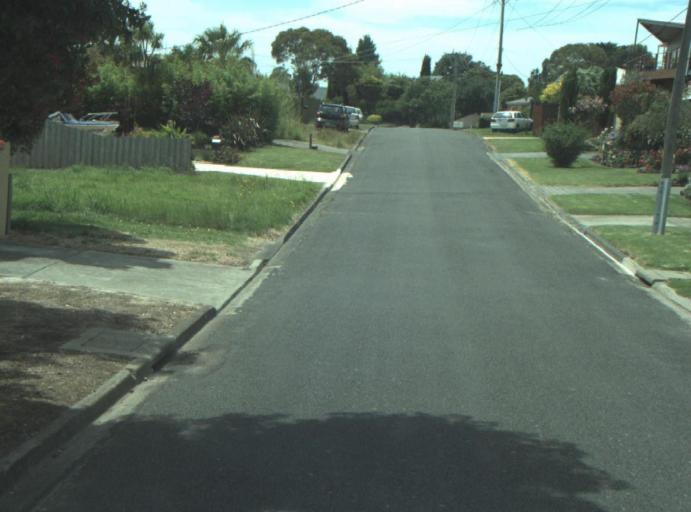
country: AU
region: Victoria
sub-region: Greater Geelong
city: Clifton Springs
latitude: -38.1595
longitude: 144.5574
